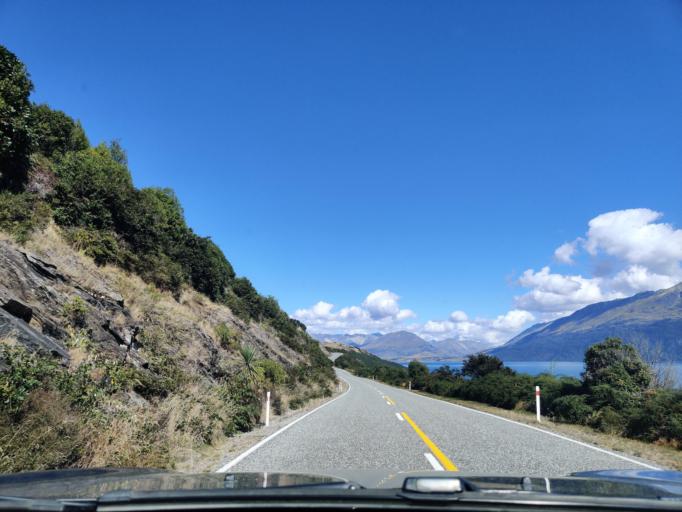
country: NZ
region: Otago
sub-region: Queenstown-Lakes District
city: Queenstown
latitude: -44.9572
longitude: 168.4380
